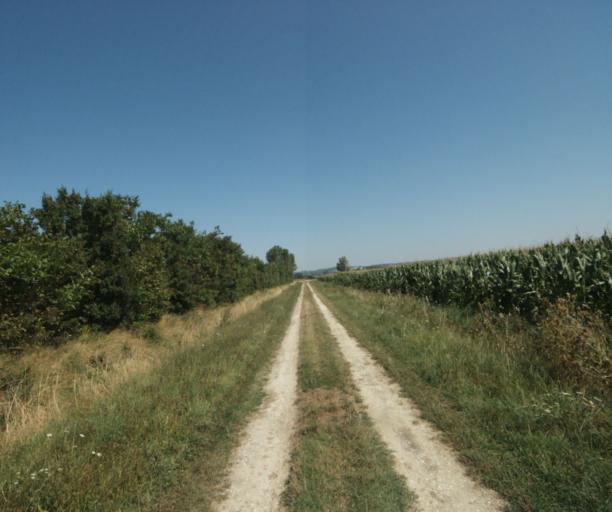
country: FR
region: Midi-Pyrenees
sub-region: Departement de la Haute-Garonne
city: Revel
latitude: 43.5104
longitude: 1.9620
